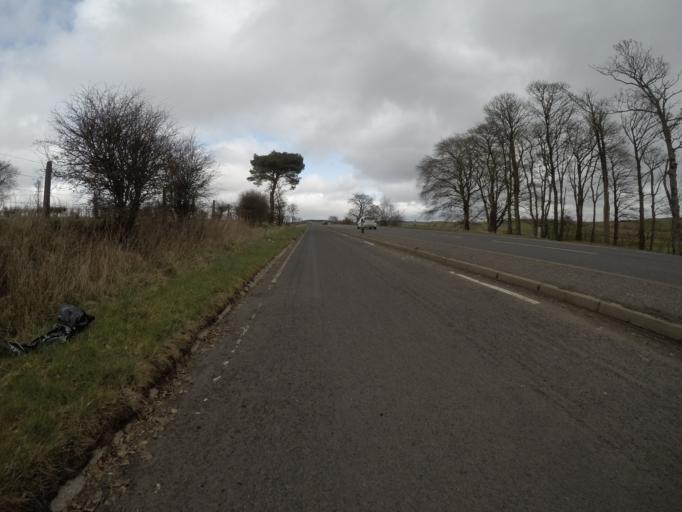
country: GB
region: Scotland
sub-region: East Ayrshire
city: Galston
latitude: 55.6852
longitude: -4.4168
